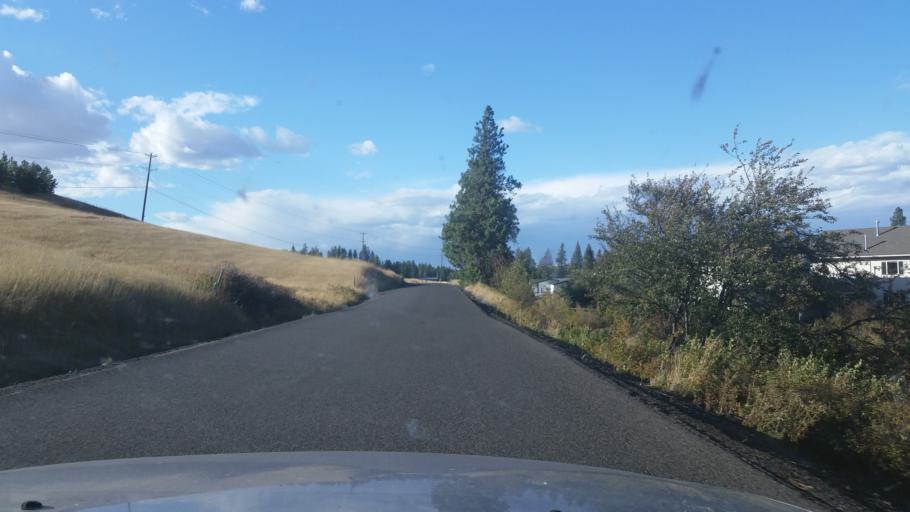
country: US
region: Washington
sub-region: Spokane County
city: Cheney
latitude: 47.5170
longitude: -117.5743
